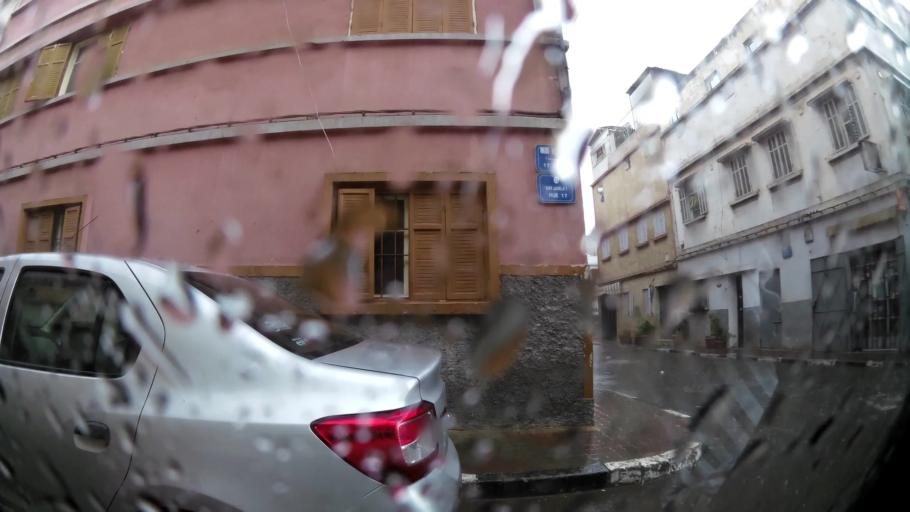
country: MA
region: Grand Casablanca
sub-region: Casablanca
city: Casablanca
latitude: 33.5489
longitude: -7.5801
